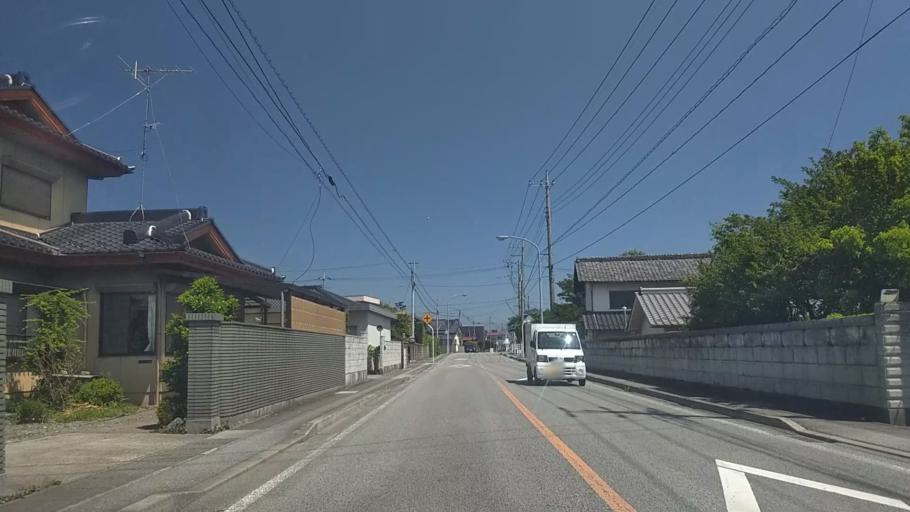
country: JP
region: Yamanashi
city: Ryuo
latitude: 35.6496
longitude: 138.4634
